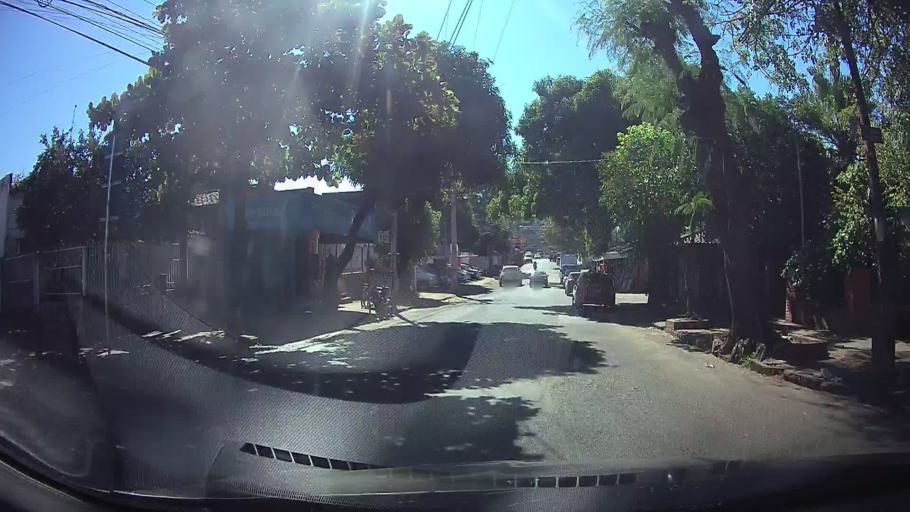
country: PY
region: Central
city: Lambare
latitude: -25.3186
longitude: -57.5727
